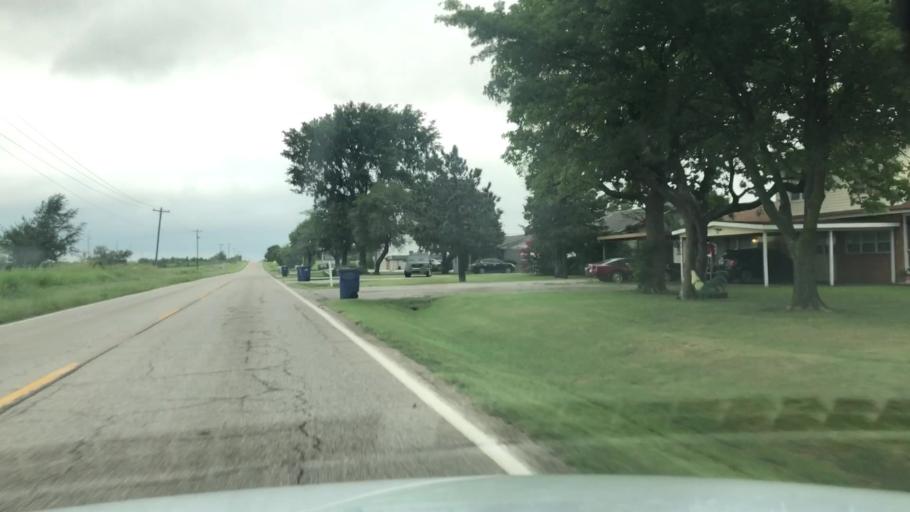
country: US
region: Oklahoma
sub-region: Nowata County
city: Nowata
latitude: 36.7059
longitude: -95.6527
